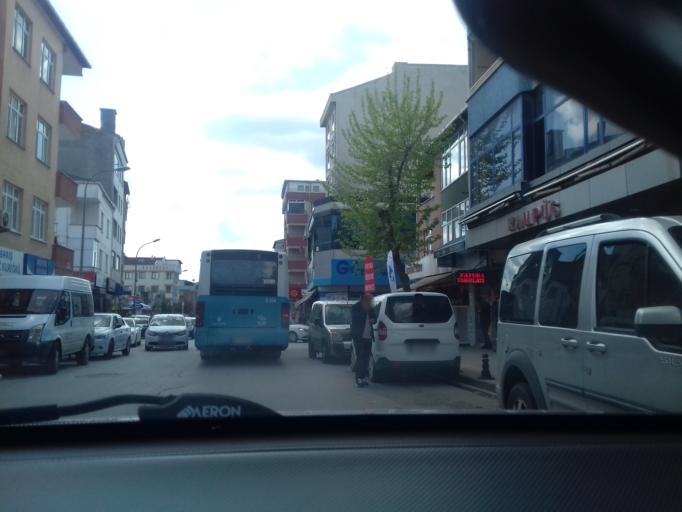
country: TR
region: Istanbul
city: Pendik
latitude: 40.8816
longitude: 29.2868
